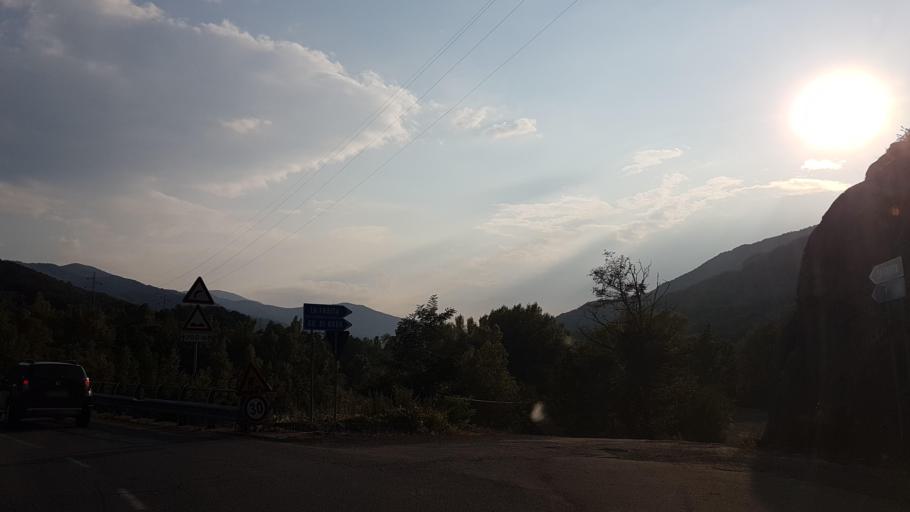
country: IT
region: Emilia-Romagna
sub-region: Provincia di Parma
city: Stazione Valmozzola
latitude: 44.5682
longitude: 9.9437
